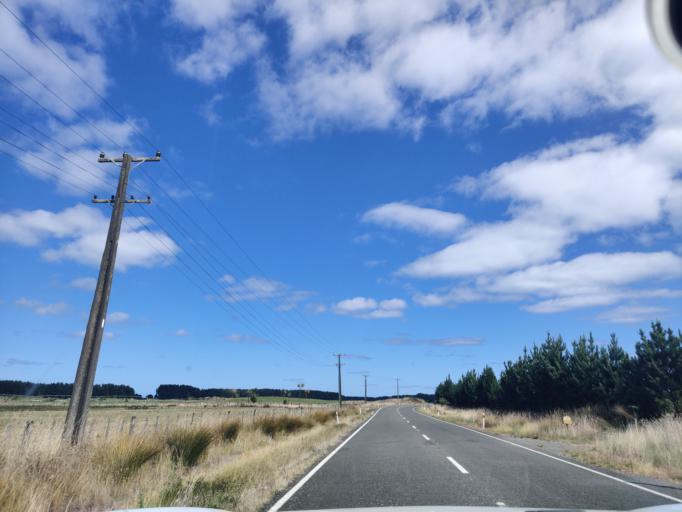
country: NZ
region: Manawatu-Wanganui
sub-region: Horowhenua District
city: Foxton
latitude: -40.3825
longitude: 175.2705
